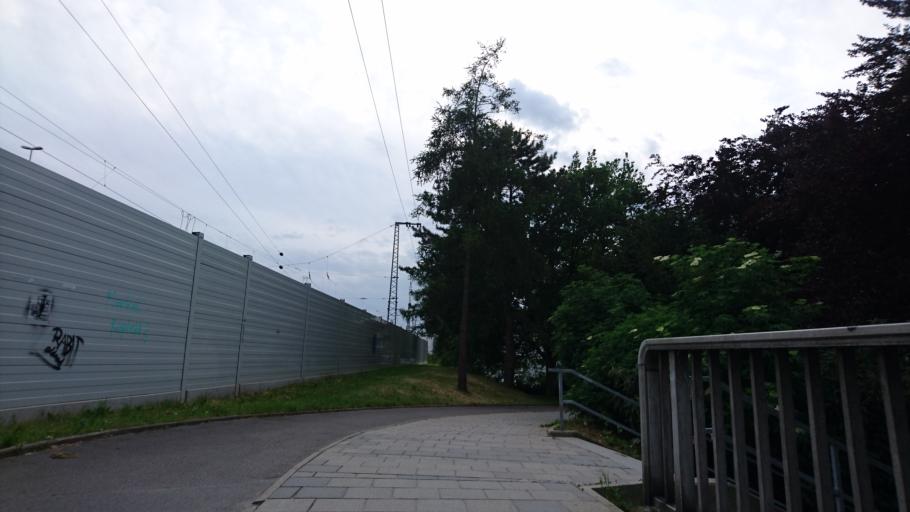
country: DE
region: Bavaria
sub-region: Upper Palatinate
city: Regensburg
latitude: 49.0119
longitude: 12.1095
